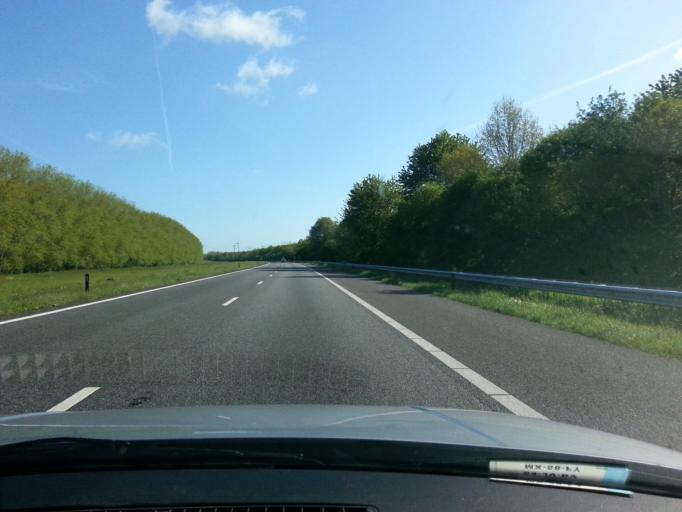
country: NL
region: Flevoland
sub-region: Gemeente Lelystad
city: Lelystad
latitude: 52.4869
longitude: 5.5168
